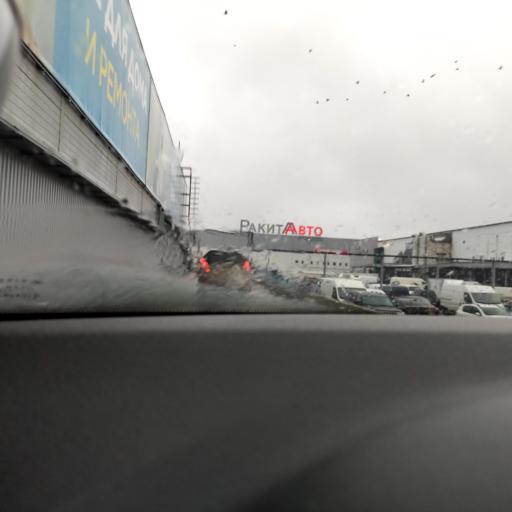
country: RU
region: Samara
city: Petra-Dubrava
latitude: 53.2770
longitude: 50.2734
